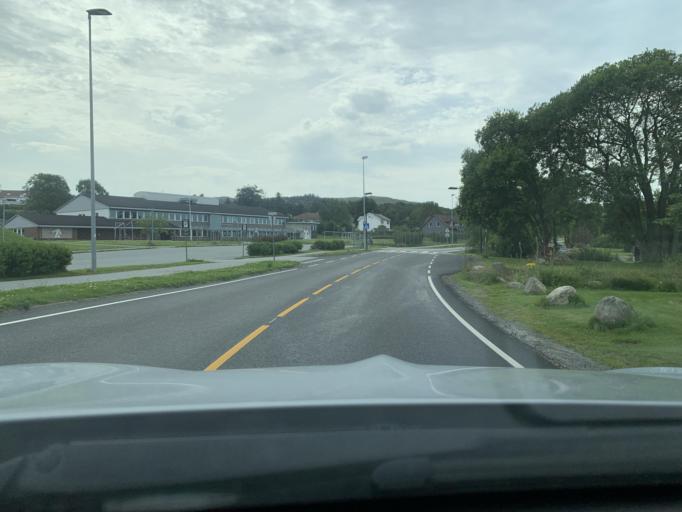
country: NO
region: Rogaland
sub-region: Sandnes
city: Sandnes
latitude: 58.7732
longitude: 5.7256
